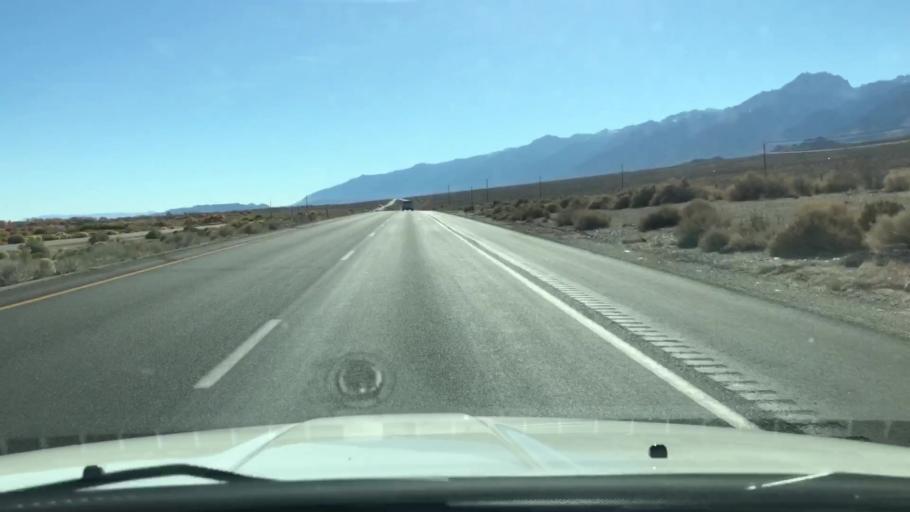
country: US
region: California
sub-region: Inyo County
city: Big Pine
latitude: 36.8799
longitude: -118.2396
